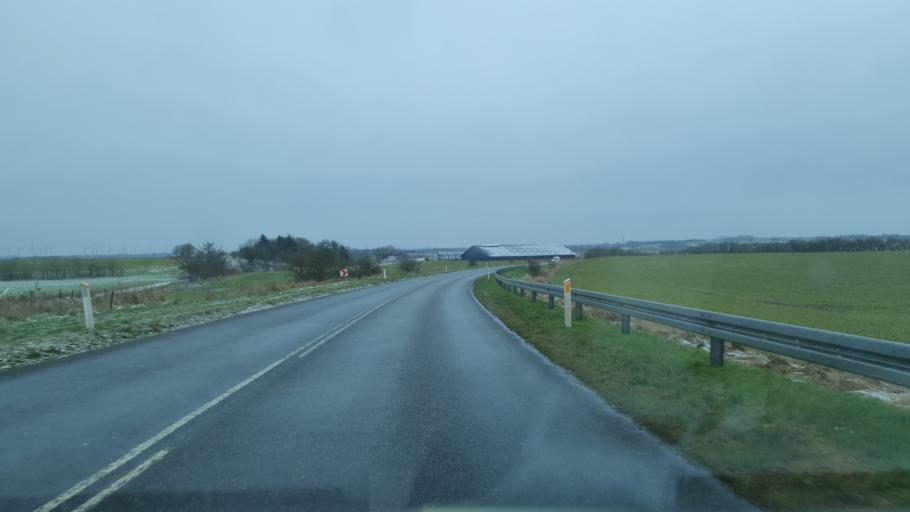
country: DK
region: North Denmark
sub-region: Jammerbugt Kommune
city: Brovst
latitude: 57.1257
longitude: 9.4858
